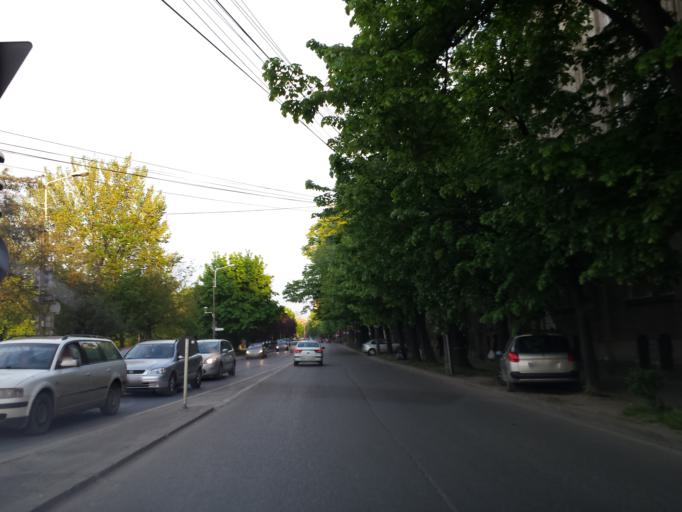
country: RO
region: Timis
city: Timisoara
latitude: 45.7492
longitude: 21.2203
